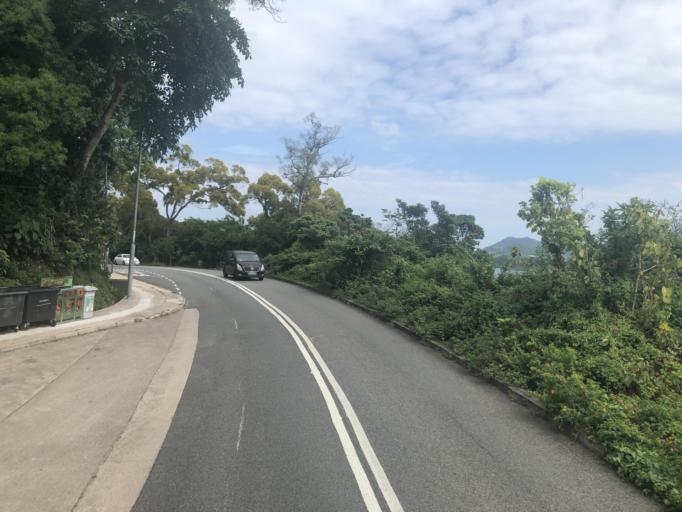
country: HK
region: Sai Kung
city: Sai Kung
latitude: 22.3887
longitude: 114.2929
